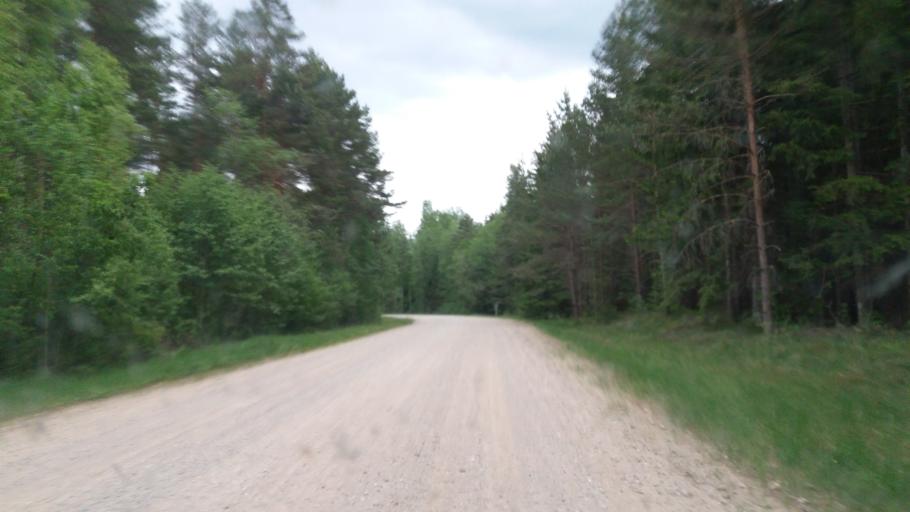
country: LV
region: Kuldigas Rajons
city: Kuldiga
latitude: 57.1744
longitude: 22.0930
